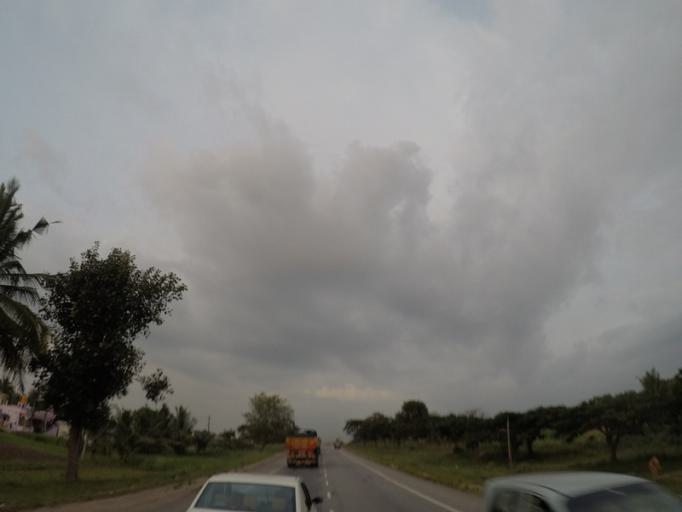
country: IN
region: Karnataka
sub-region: Hassan
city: Hassan
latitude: 12.9996
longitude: 76.1290
